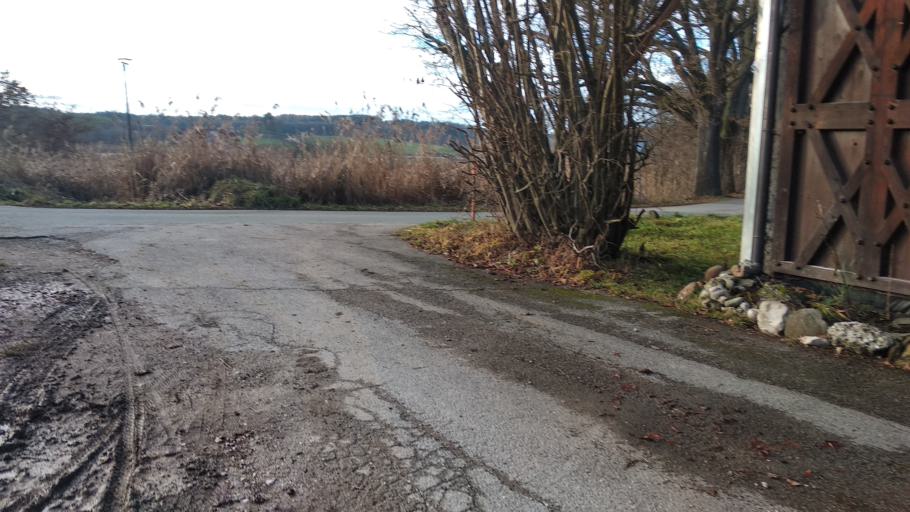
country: DE
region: Bavaria
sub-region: Upper Bavaria
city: Ebersberg
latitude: 48.0805
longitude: 11.9499
